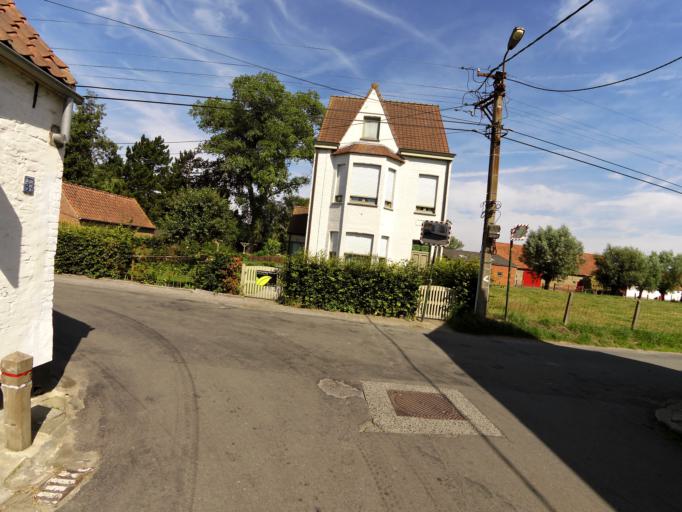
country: BE
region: Flanders
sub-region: Provincie West-Vlaanderen
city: Damme
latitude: 51.2785
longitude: 3.2940
